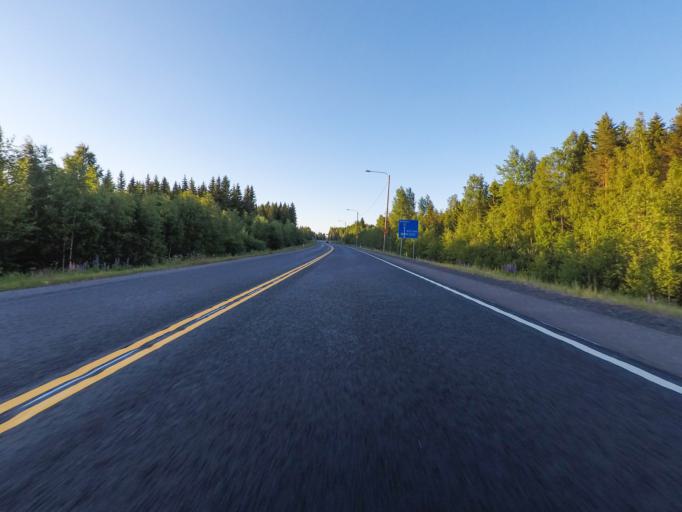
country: FI
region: Southern Savonia
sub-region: Mikkeli
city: Maentyharju
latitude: 61.5770
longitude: 27.0006
